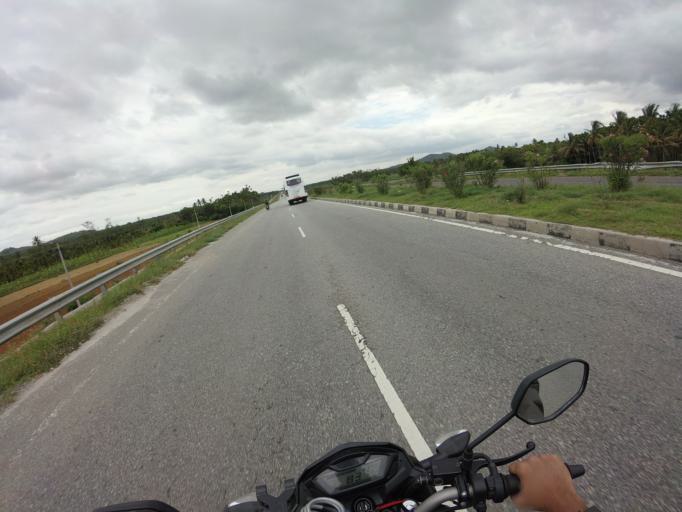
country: IN
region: Karnataka
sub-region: Tumkur
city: Kunigal
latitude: 13.0050
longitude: 77.0059
